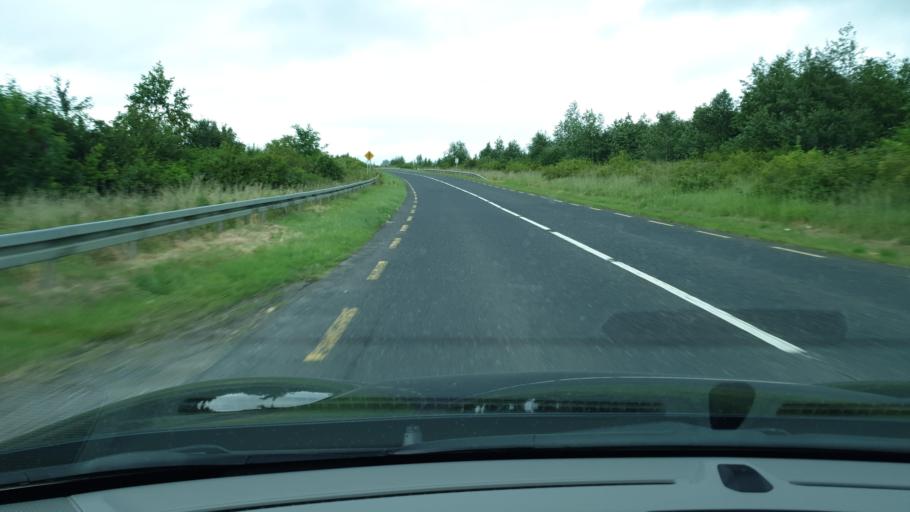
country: IE
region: Leinster
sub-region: An Mhi
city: Dunboyne
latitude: 53.4514
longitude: -6.4844
